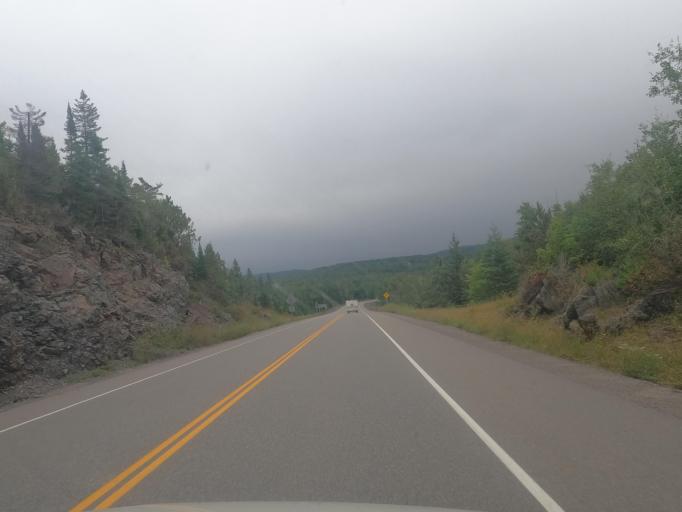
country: CA
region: Ontario
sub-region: Algoma
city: Sault Ste. Marie
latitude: 46.8531
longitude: -84.3709
